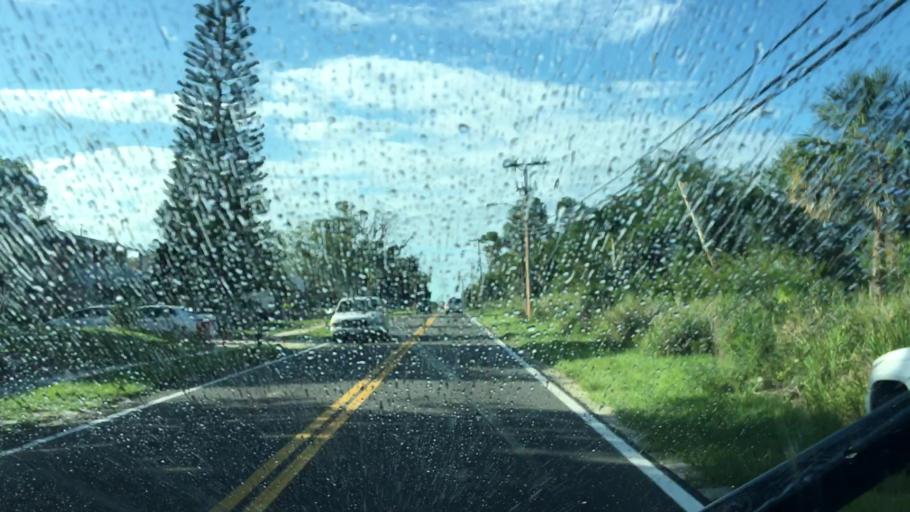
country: US
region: Florida
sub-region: Brevard County
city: Mims
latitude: 28.6221
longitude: -80.8603
